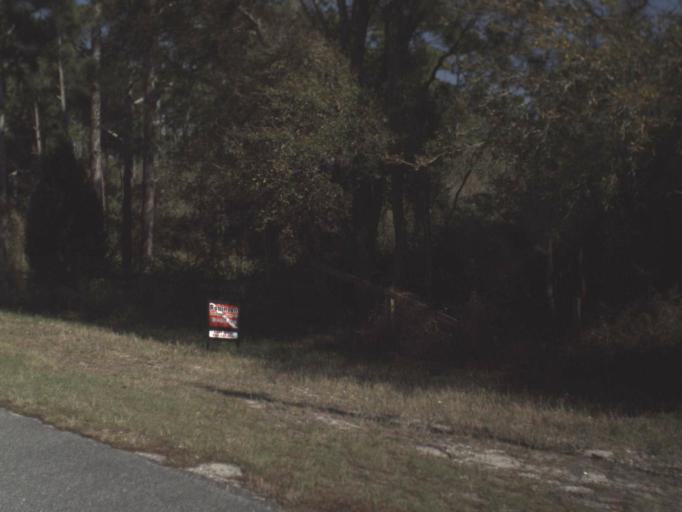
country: US
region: Florida
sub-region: Franklin County
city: Carrabelle
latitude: 29.7899
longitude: -84.7640
